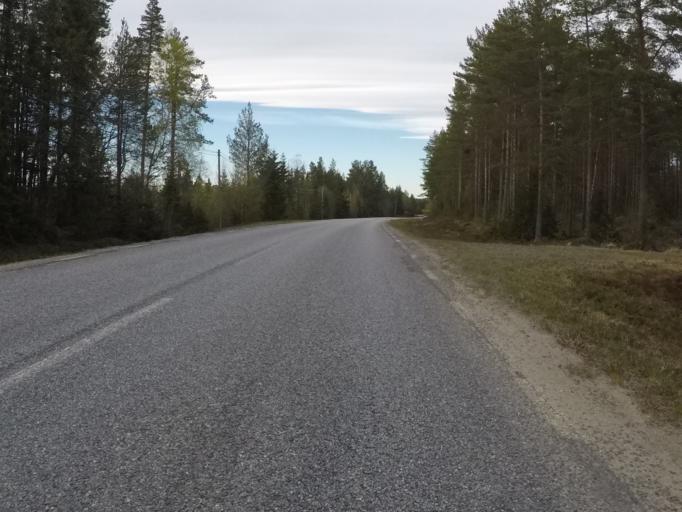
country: SE
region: Vaesterbotten
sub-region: Umea Kommun
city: Saevar
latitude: 63.9364
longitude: 20.7835
